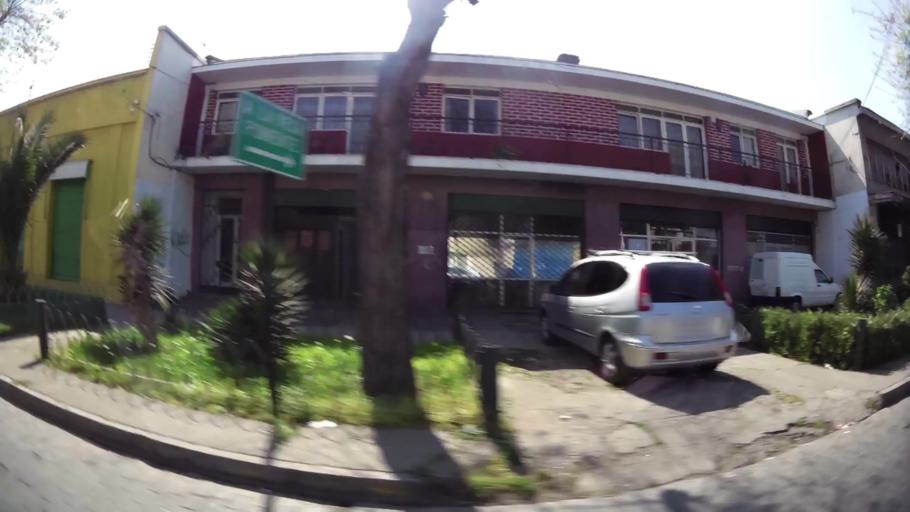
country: CL
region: Santiago Metropolitan
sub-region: Provincia de Santiago
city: Santiago
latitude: -33.4665
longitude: -70.6754
